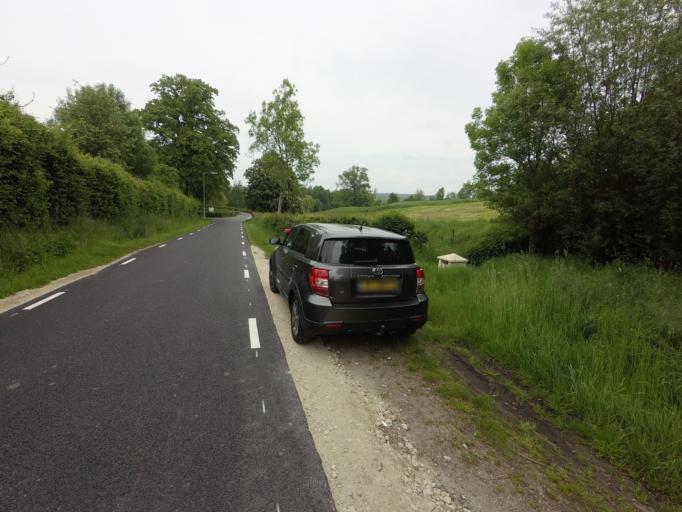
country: BE
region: Wallonia
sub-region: Province de Liege
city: Plombieres
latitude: 50.7609
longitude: 5.9117
